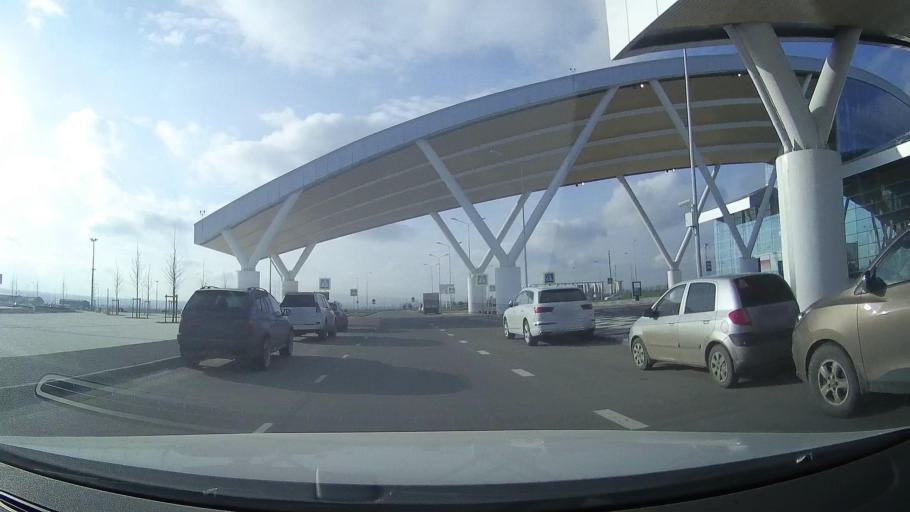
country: RU
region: Rostov
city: Grushevskaya
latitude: 47.4877
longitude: 39.9298
